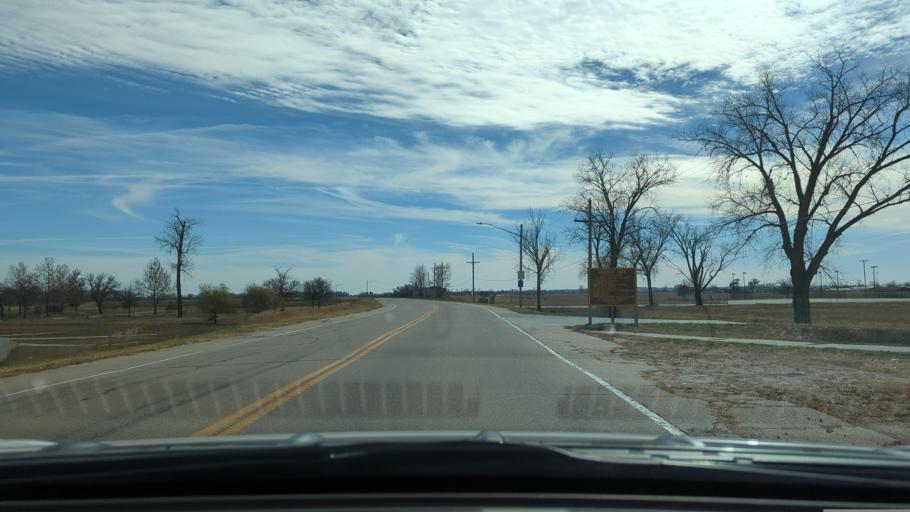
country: US
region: Nebraska
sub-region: Sarpy County
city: Bellevue
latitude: 41.1365
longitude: -95.8846
